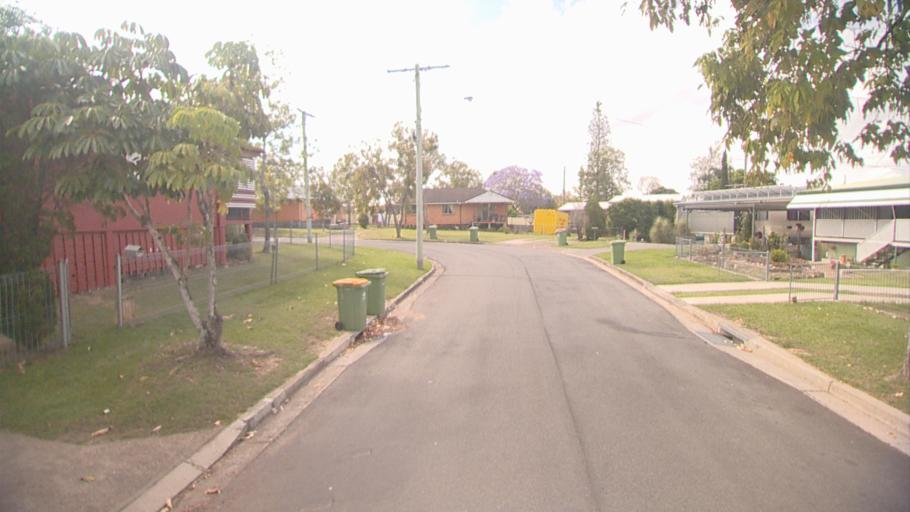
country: AU
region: Queensland
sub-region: Logan
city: Springwood
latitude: -27.6259
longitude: 153.1254
